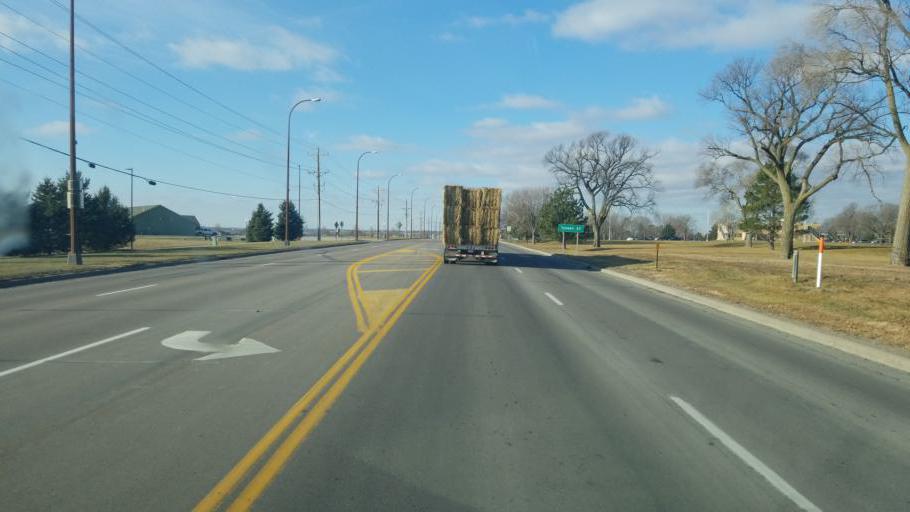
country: US
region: South Dakota
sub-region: Yankton County
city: Yankton
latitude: 42.9092
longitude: -97.4004
